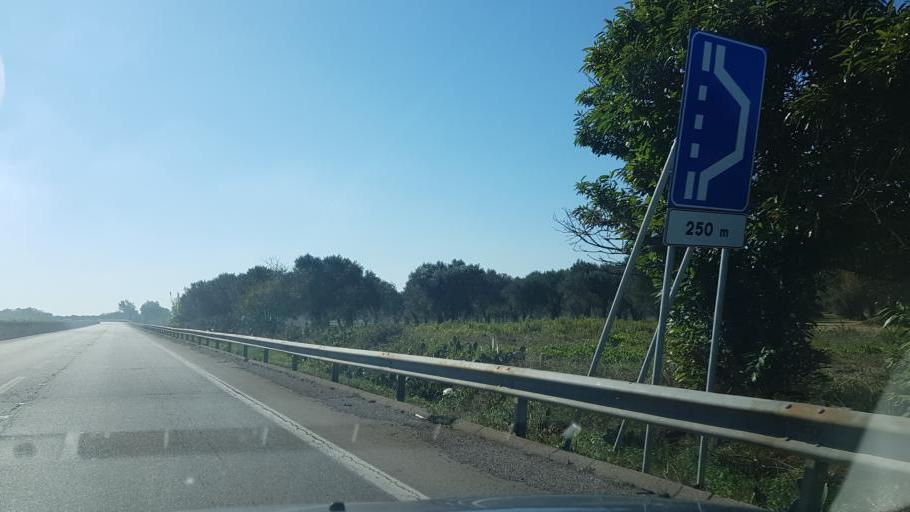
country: IT
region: Apulia
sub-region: Provincia di Brindisi
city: Tuturano
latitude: 40.5453
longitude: 17.9997
